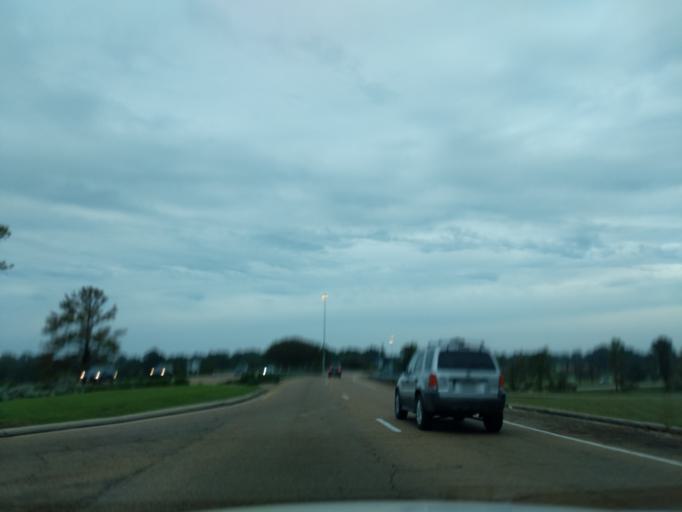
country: US
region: Mississippi
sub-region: Warren County
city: Vicksburg
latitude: 32.3171
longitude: -90.8771
